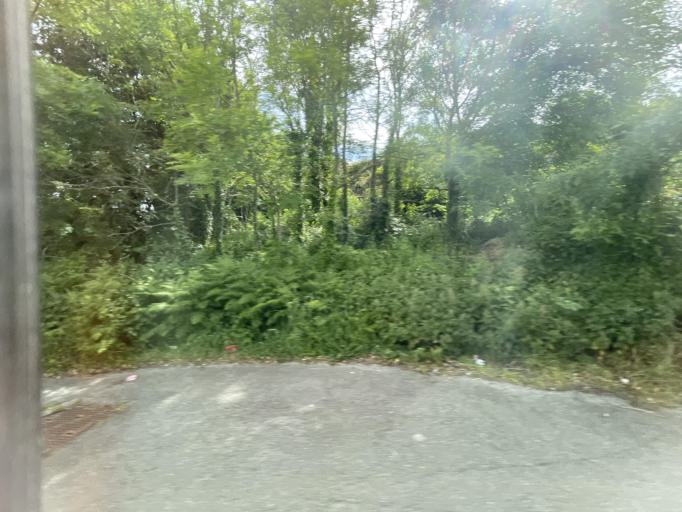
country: GB
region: Wales
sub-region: Anglesey
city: Llanfachraeth
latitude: 53.2626
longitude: -4.4466
